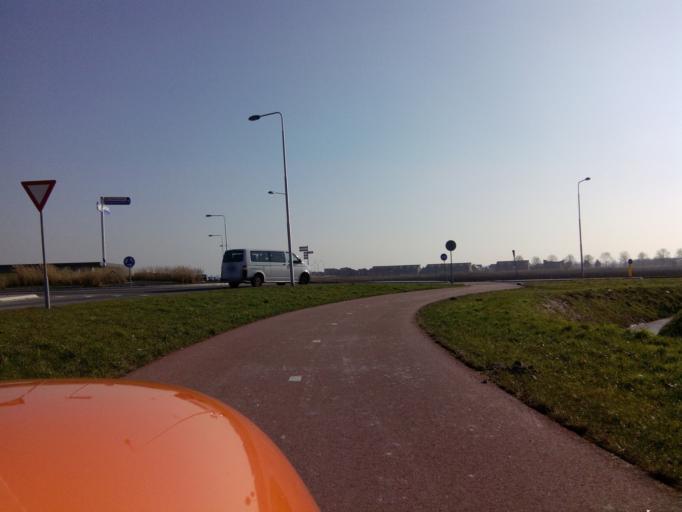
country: NL
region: Flevoland
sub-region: Gemeente Zeewolde
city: Zeewolde
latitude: 52.3481
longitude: 5.5123
